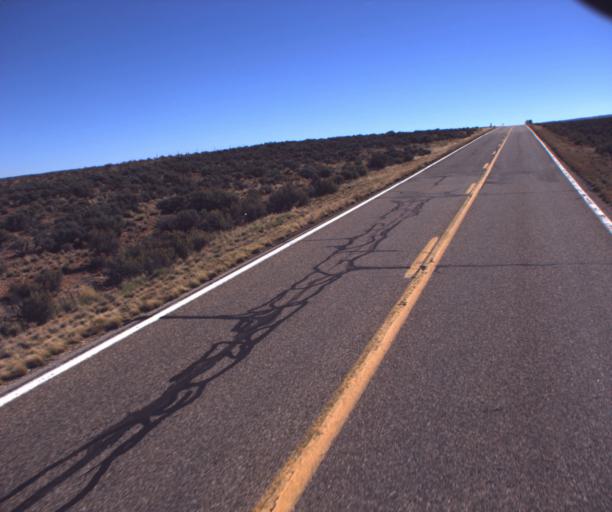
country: US
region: Arizona
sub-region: Coconino County
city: Fredonia
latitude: 36.8938
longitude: -112.3611
